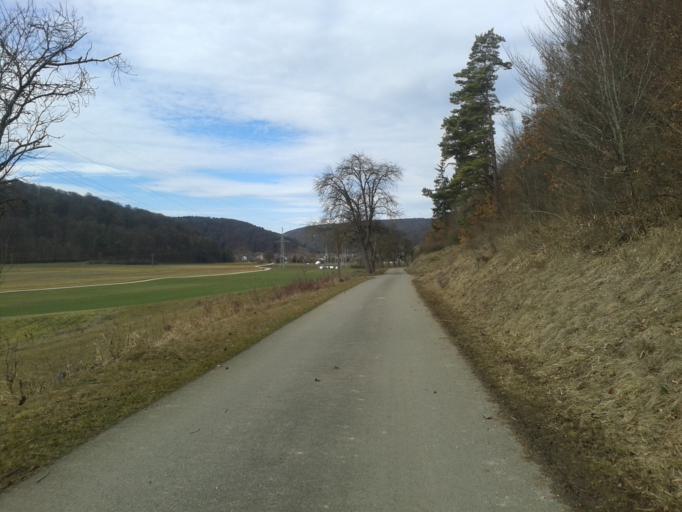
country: DE
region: Baden-Wuerttemberg
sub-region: Tuebingen Region
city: Schelklingen
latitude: 48.3559
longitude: 9.7348
